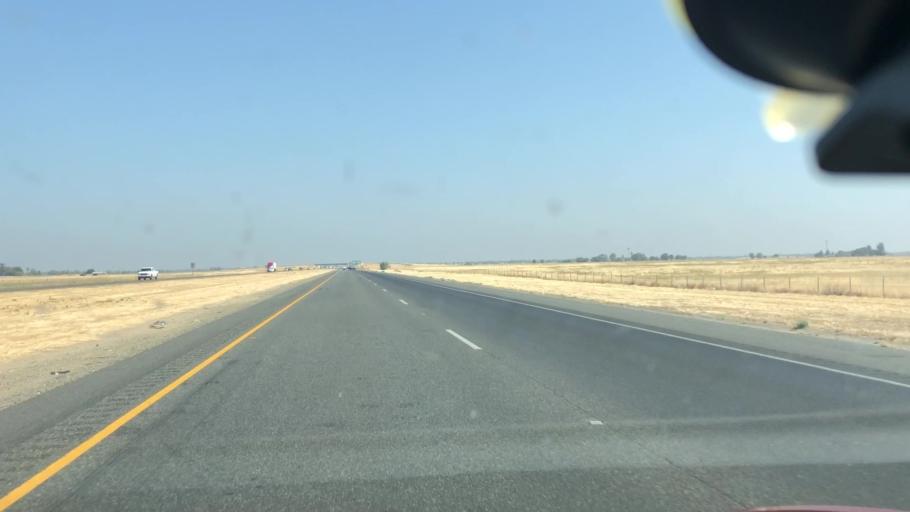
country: US
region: California
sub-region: Sacramento County
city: Laguna
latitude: 38.3627
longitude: -121.4740
